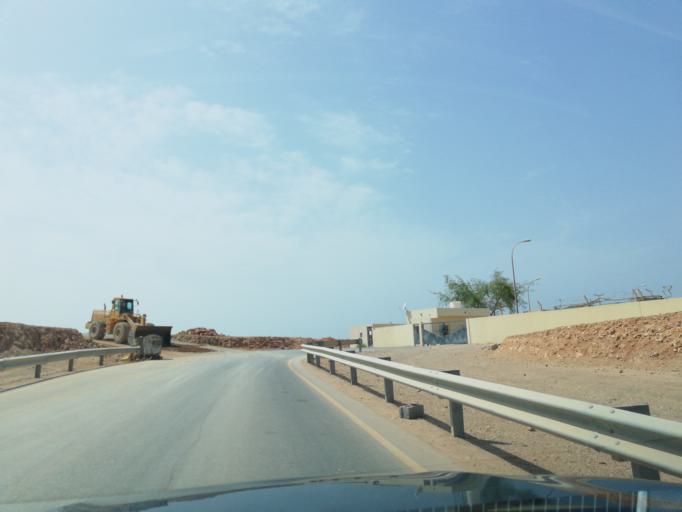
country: OM
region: Muhafazat Masqat
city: Bawshar
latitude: 23.5551
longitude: 58.3374
